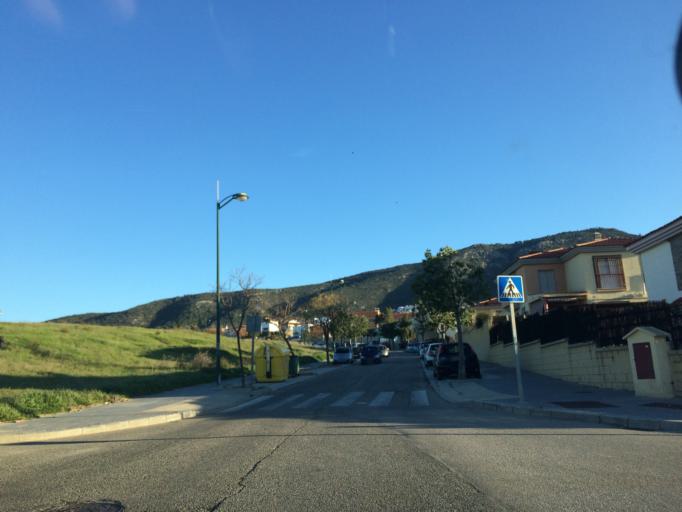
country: ES
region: Andalusia
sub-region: Provincia de Malaga
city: Alhaurin de la Torre
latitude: 36.6677
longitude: -4.5357
